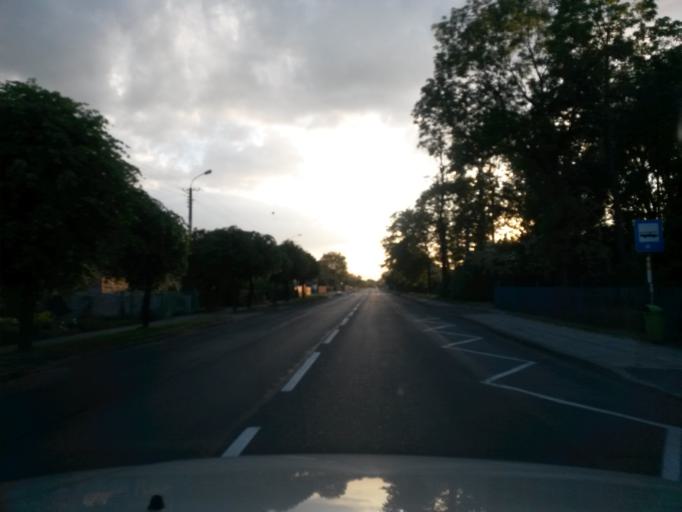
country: PL
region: Lodz Voivodeship
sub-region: Powiat wielunski
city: Mokrsko
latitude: 51.2629
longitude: 18.4657
